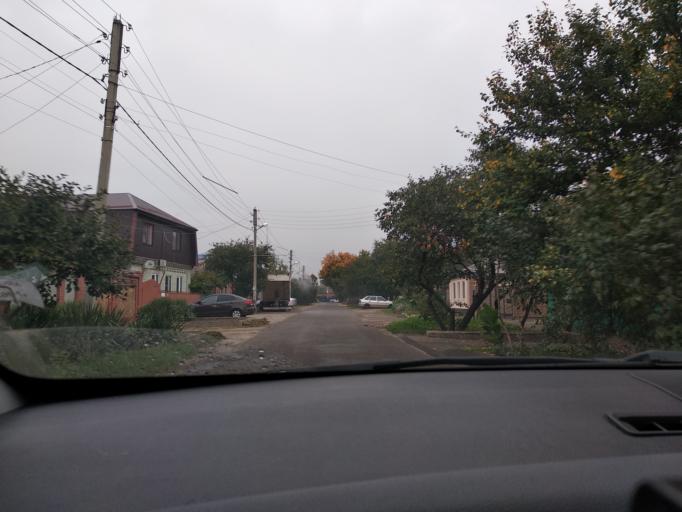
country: RU
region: Krasnodarskiy
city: Krasnodar
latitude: 45.0156
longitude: 39.0001
